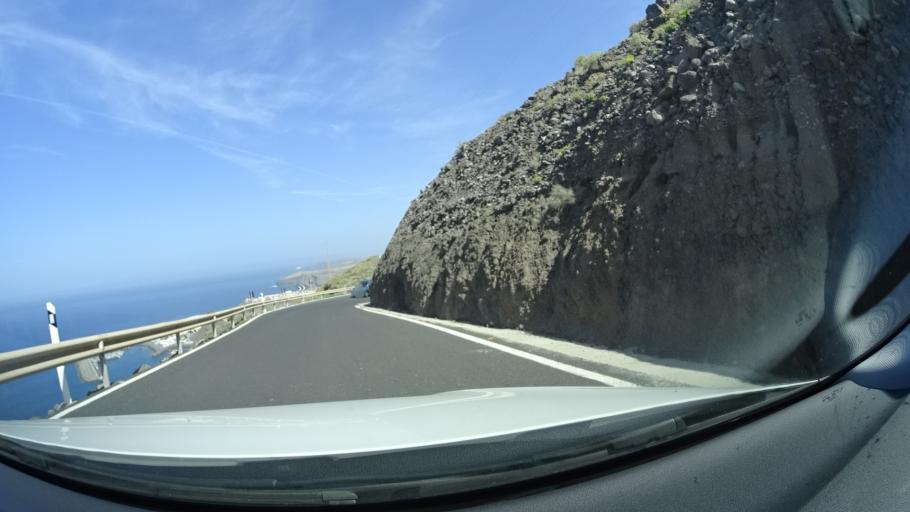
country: ES
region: Canary Islands
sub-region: Provincia de Las Palmas
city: Agaete
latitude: 28.0913
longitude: -15.7066
